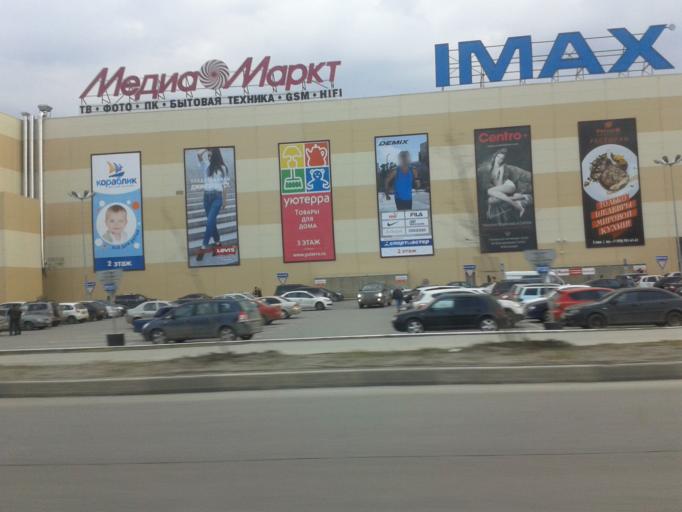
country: RU
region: Rjazan
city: Ryazan'
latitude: 54.6353
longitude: 39.6904
